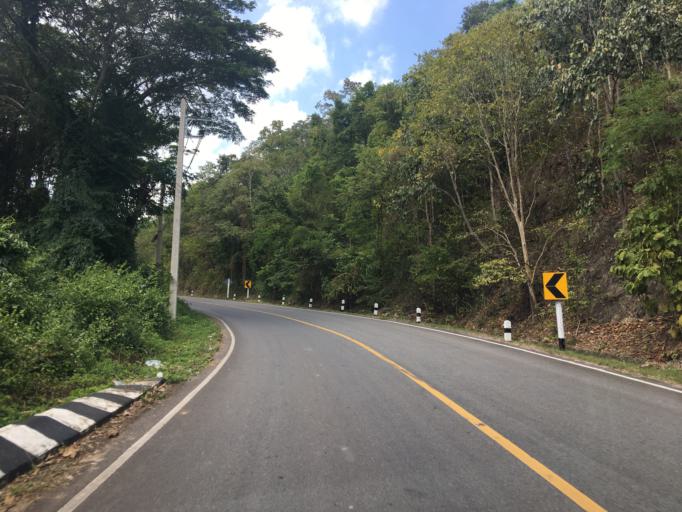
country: TH
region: Nan
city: Nan
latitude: 18.8641
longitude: 100.6328
